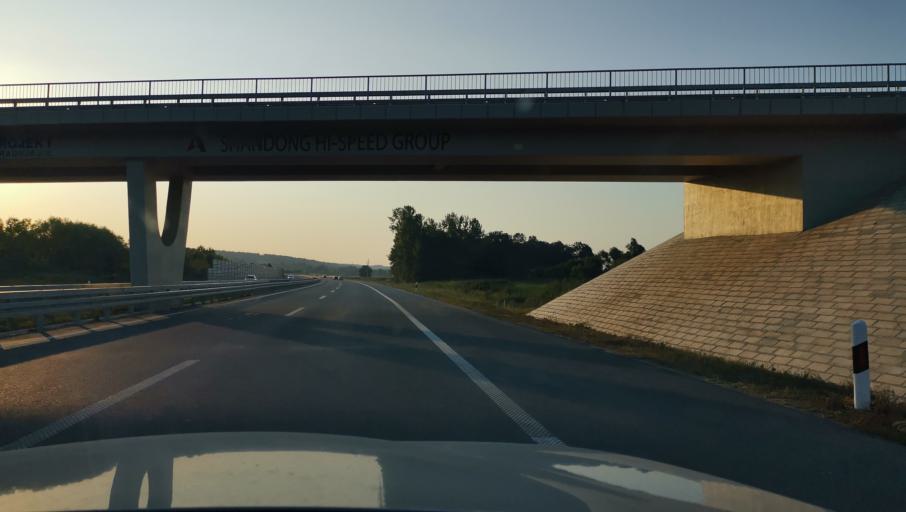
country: RS
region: Central Serbia
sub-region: Kolubarski Okrug
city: Ljig
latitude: 44.2849
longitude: 20.2532
